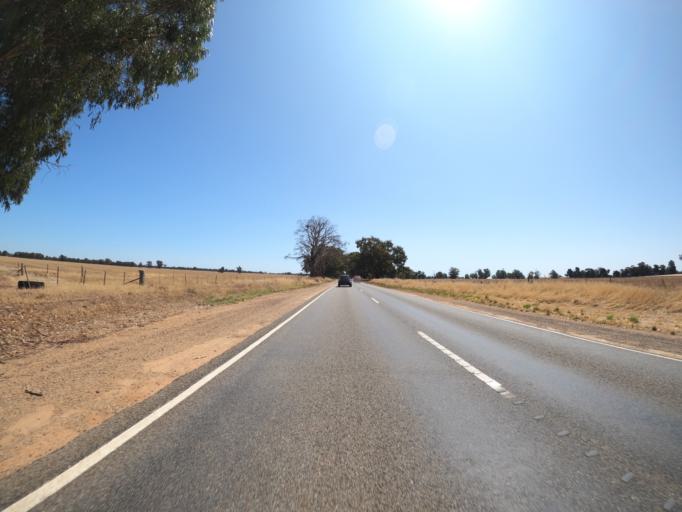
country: AU
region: Victoria
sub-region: Moira
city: Yarrawonga
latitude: -36.0240
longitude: 146.1121
